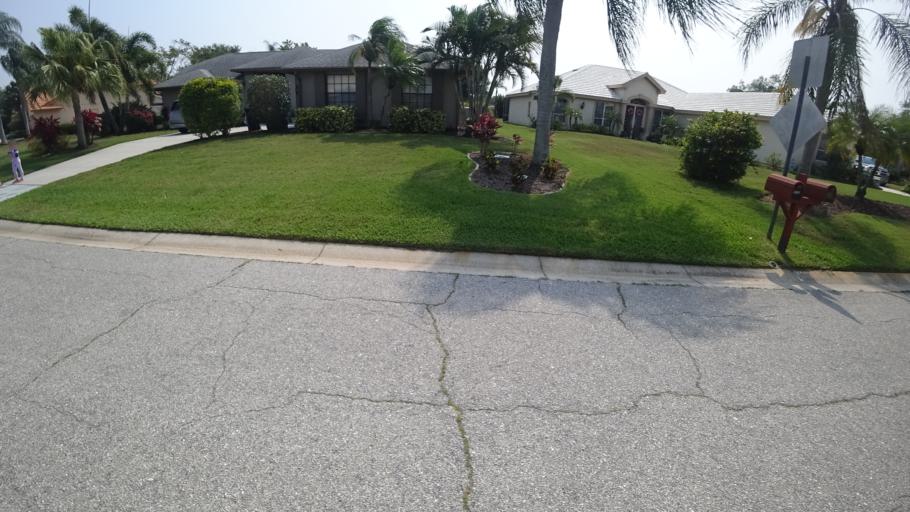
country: US
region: Florida
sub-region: Manatee County
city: Samoset
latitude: 27.4503
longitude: -82.5063
